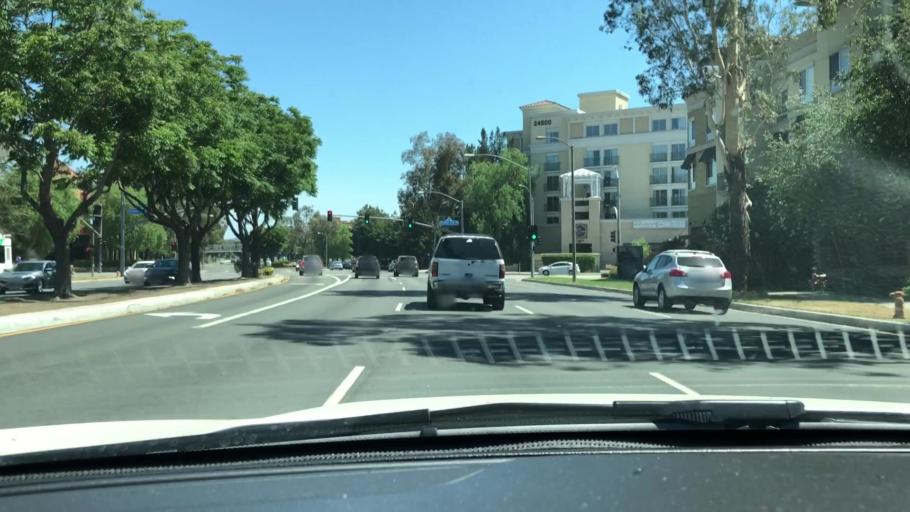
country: US
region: California
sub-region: Los Angeles County
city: Santa Clarita
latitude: 34.4185
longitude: -118.5627
